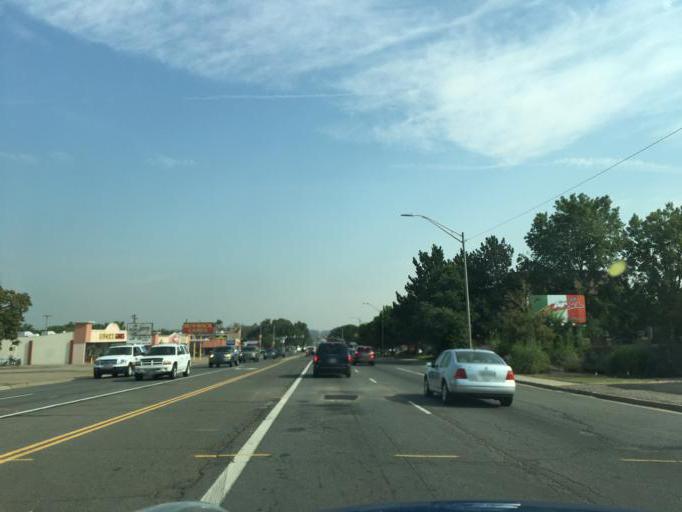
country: US
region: Colorado
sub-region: Jefferson County
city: Wheat Ridge
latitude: 39.7744
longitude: -105.0814
